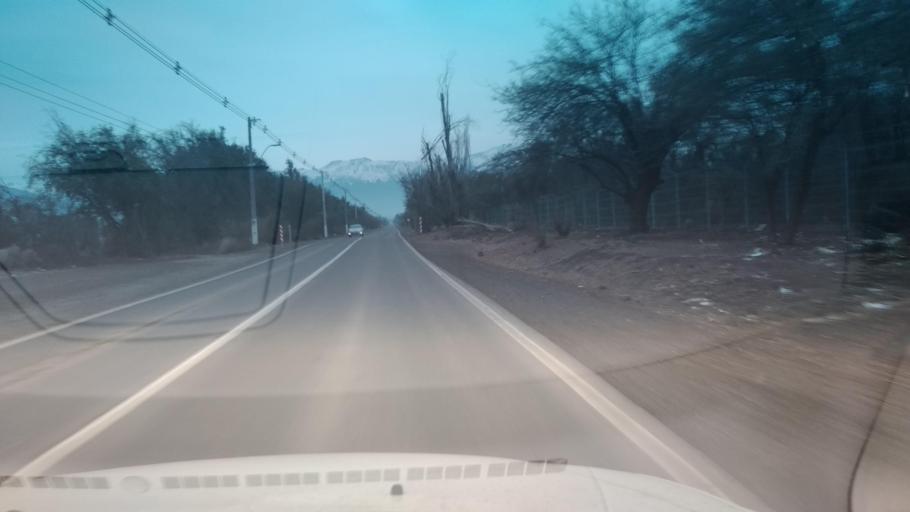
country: CL
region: Santiago Metropolitan
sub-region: Provincia de Chacabuco
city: Chicureo Abajo
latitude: -33.0924
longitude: -70.7248
